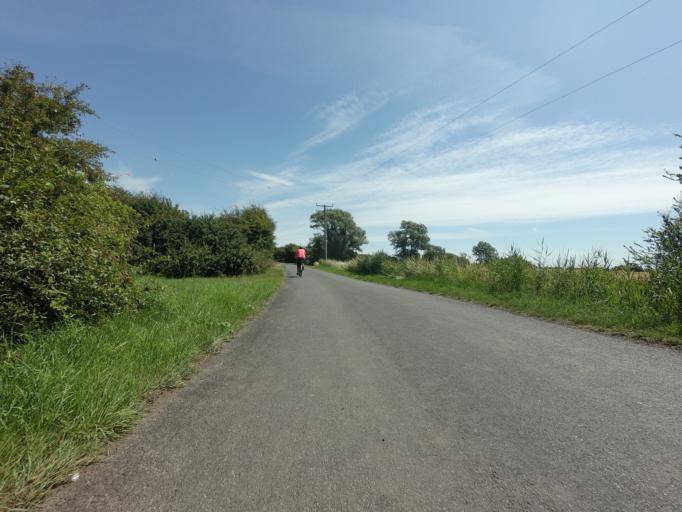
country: GB
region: England
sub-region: Kent
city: Lydd
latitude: 50.9779
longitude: 0.8499
